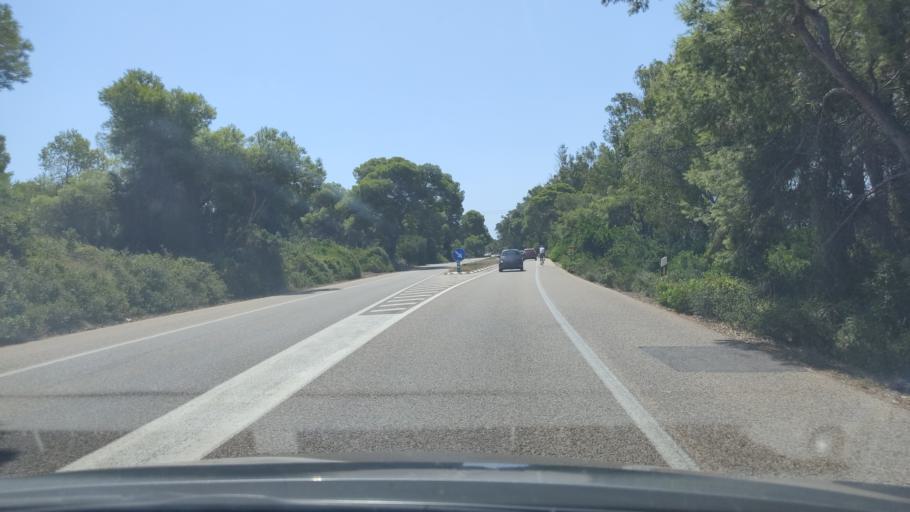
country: ES
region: Valencia
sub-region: Provincia de Valencia
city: Sollana
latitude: 39.3218
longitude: -0.3085
